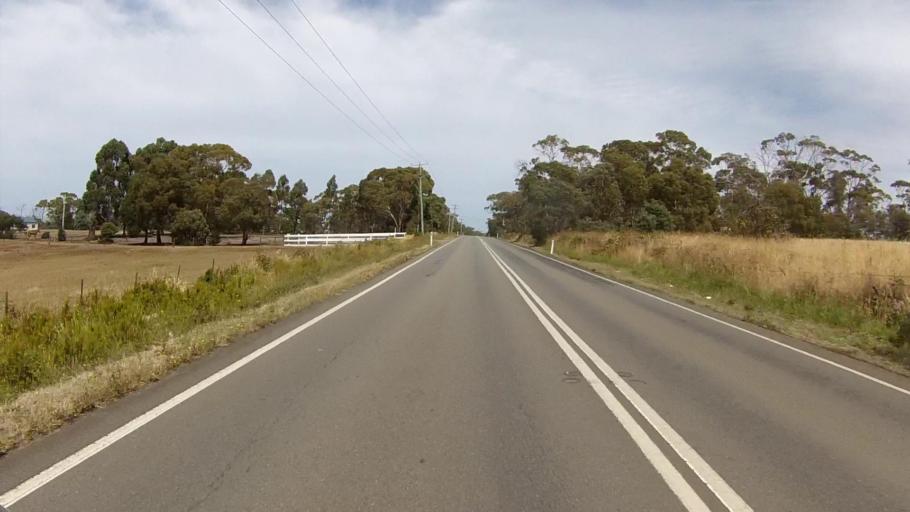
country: AU
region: Tasmania
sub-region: Clarence
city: Sandford
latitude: -43.0052
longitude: 147.4941
